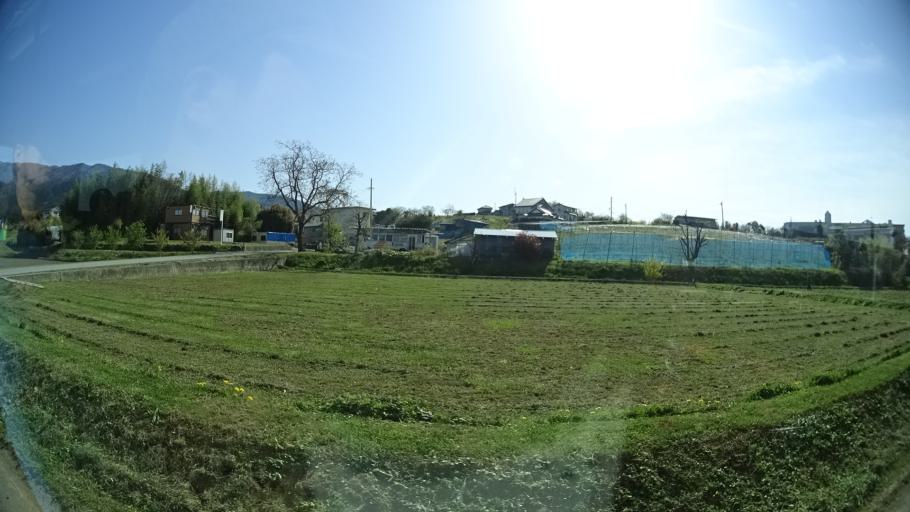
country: JP
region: Iwate
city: Ofunato
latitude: 39.0167
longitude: 141.6459
